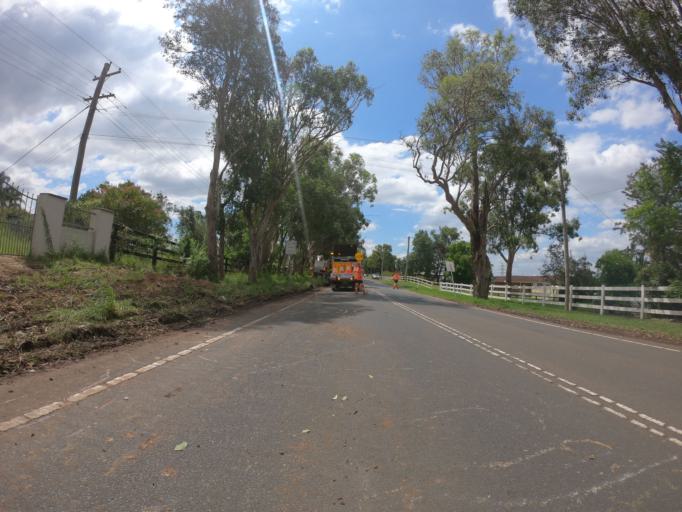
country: AU
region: New South Wales
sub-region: Penrith Municipality
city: Kingswood Park
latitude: -33.8201
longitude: 150.7606
